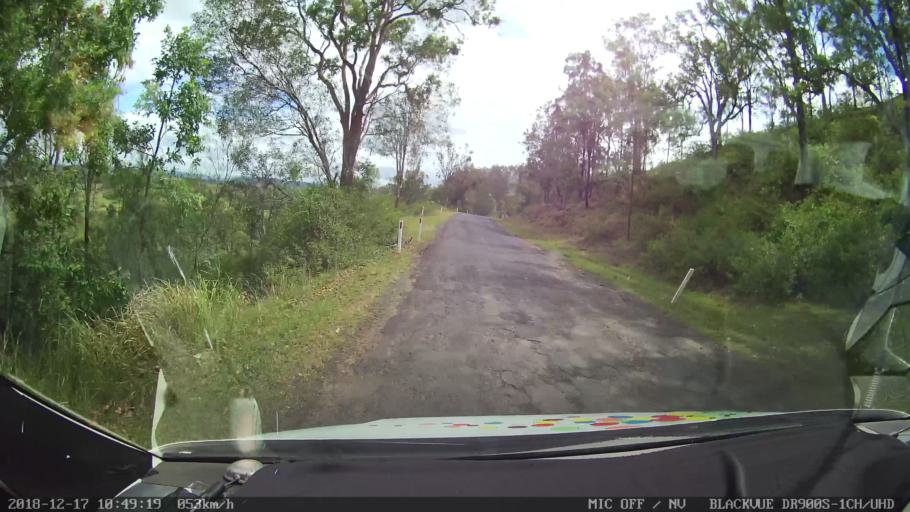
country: AU
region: New South Wales
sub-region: Clarence Valley
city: Gordon
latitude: -28.8665
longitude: 152.5730
